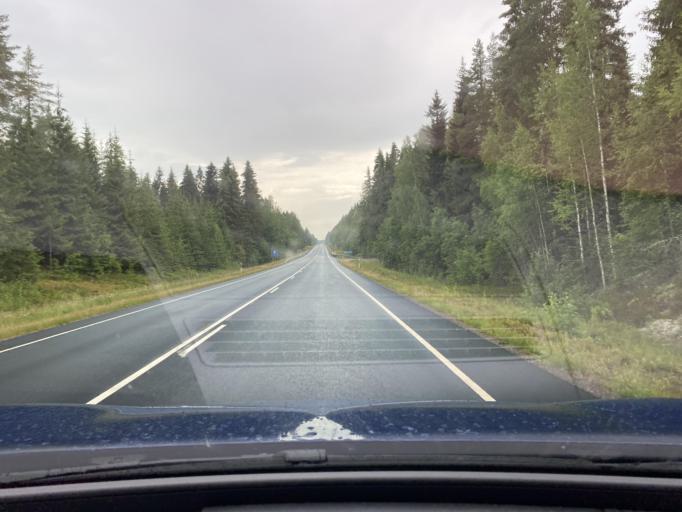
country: FI
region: Central Ostrobothnia
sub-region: Kaustinen
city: Veteli
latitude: 63.4153
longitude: 23.9475
